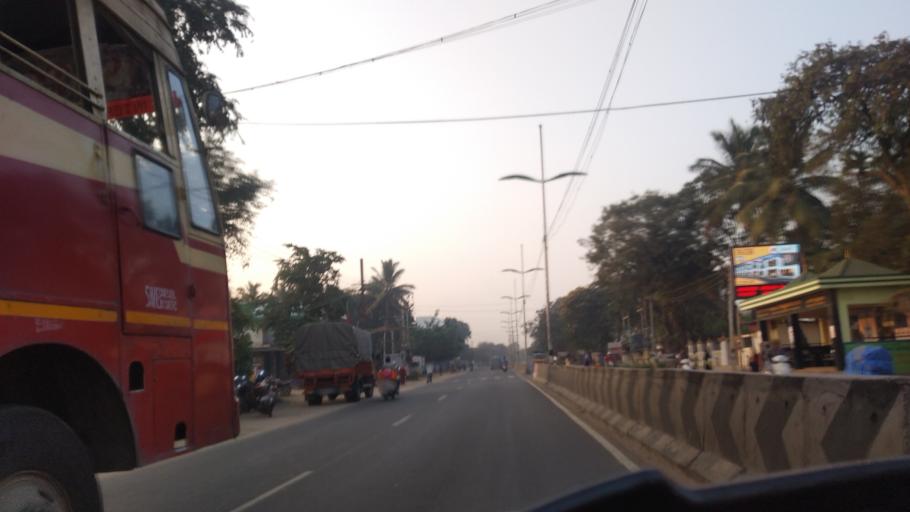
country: IN
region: Tamil Nadu
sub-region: Coimbatore
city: Perur
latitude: 10.9525
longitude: 76.9536
